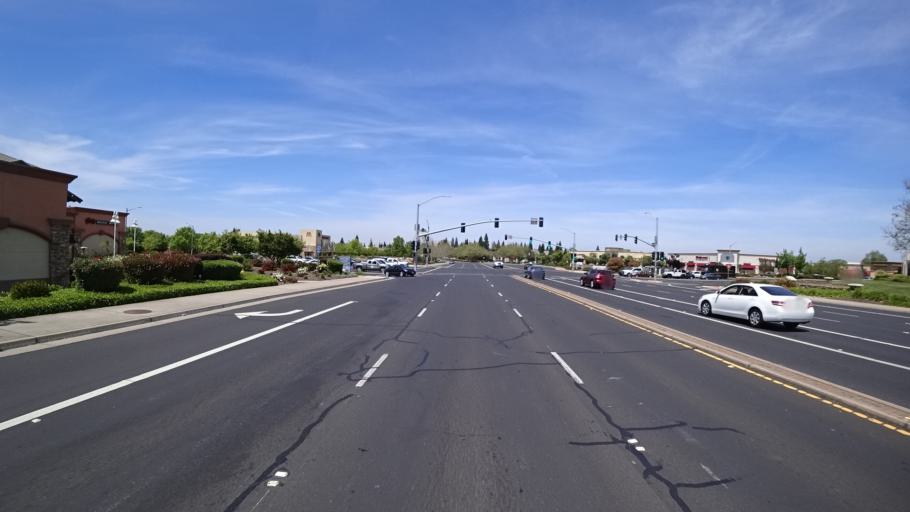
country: US
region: California
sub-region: Placer County
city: Rocklin
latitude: 38.8042
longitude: -121.2726
